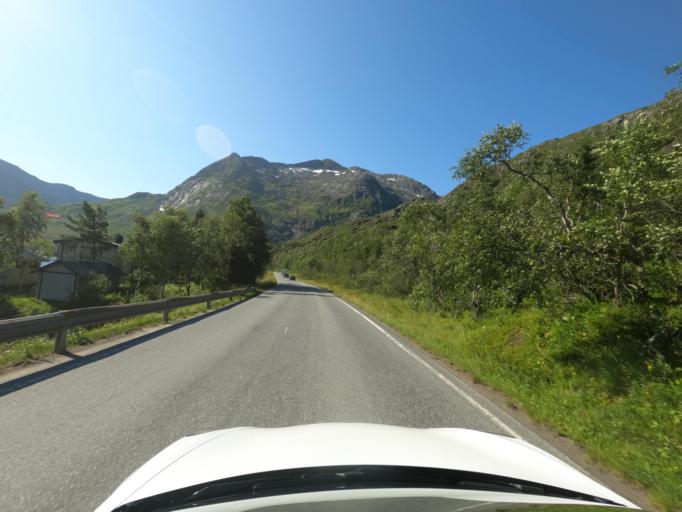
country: NO
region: Nordland
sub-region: Lodingen
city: Lodingen
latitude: 68.5393
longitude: 15.7242
